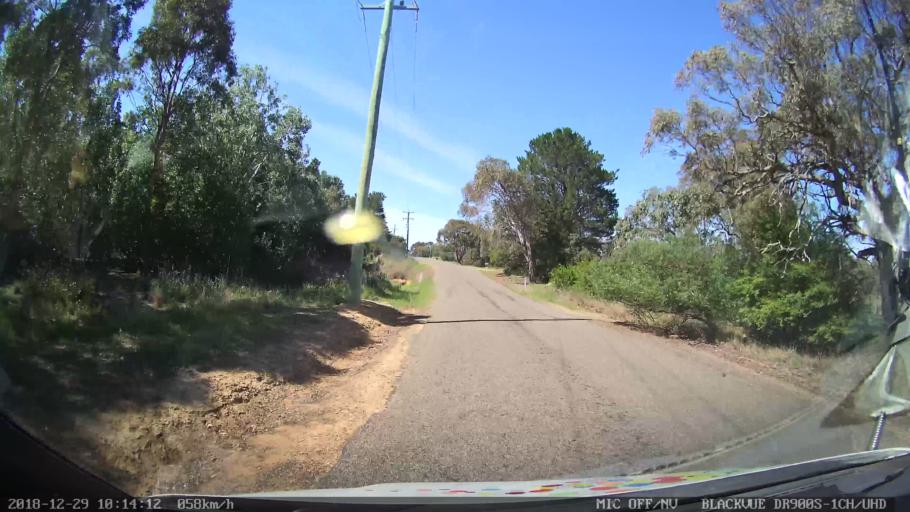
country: AU
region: New South Wales
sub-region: Yass Valley
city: Gundaroo
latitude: -34.9102
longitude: 149.4396
